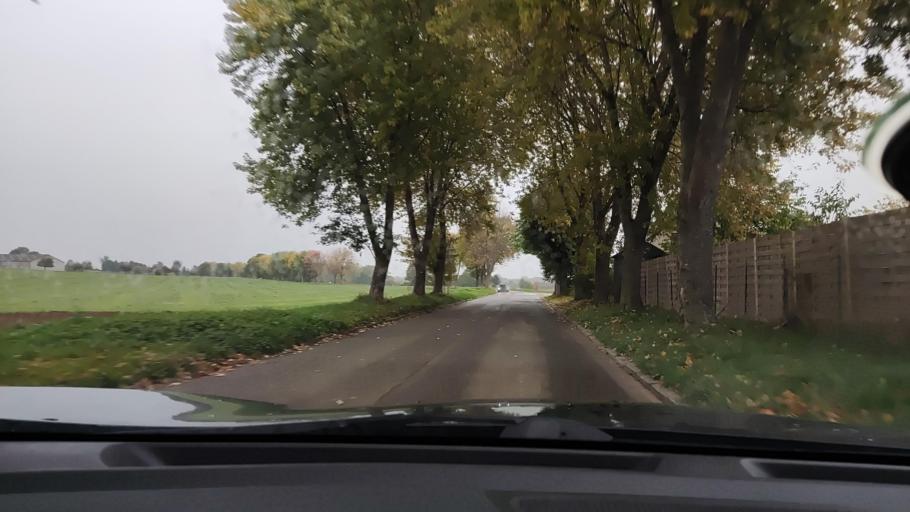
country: BE
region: Wallonia
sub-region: Province du Brabant Wallon
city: Jodoigne
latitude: 50.7063
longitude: 4.9421
